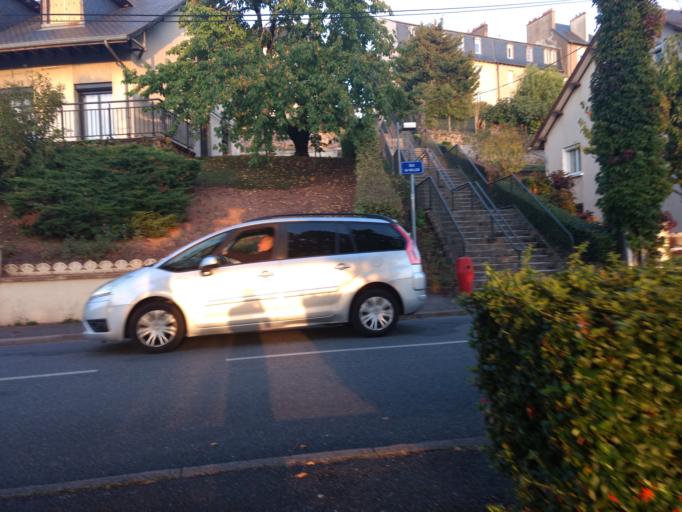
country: FR
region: Midi-Pyrenees
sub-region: Departement de l'Aveyron
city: Rodez
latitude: 44.3597
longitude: 2.5794
